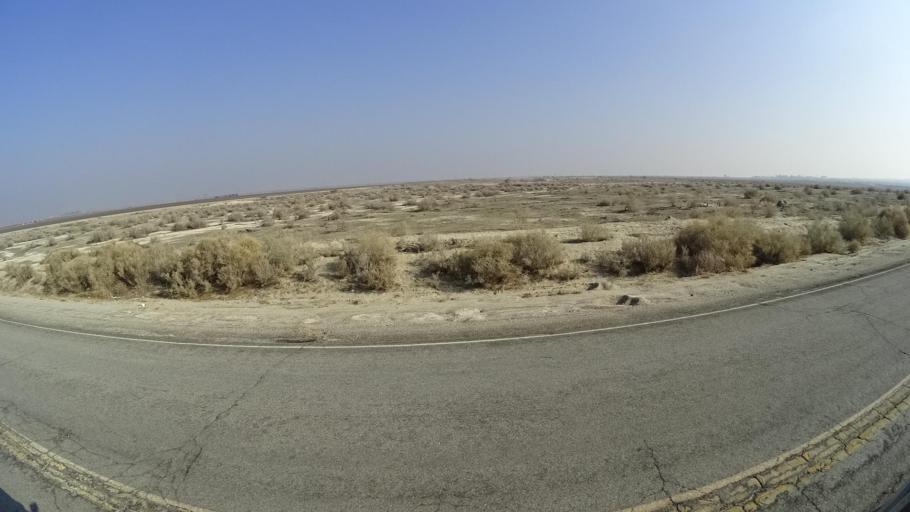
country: US
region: California
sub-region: Kern County
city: Buttonwillow
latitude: 35.3119
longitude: -119.3767
